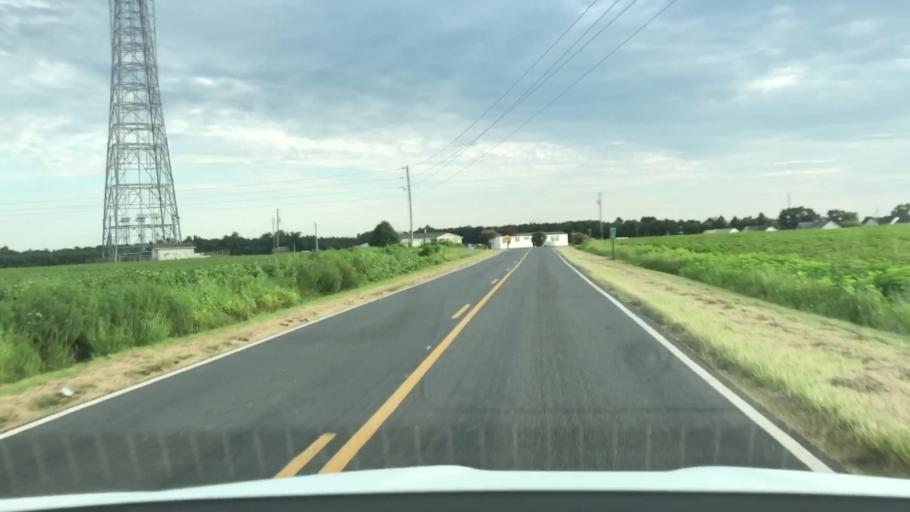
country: US
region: North Carolina
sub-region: Jones County
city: Trenton
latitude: 34.9947
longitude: -77.2805
